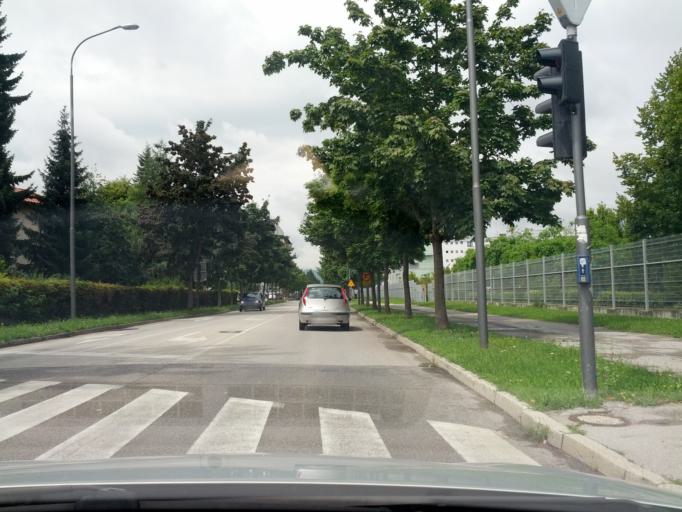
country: SI
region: Ljubljana
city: Ljubljana
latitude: 46.0708
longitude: 14.5186
